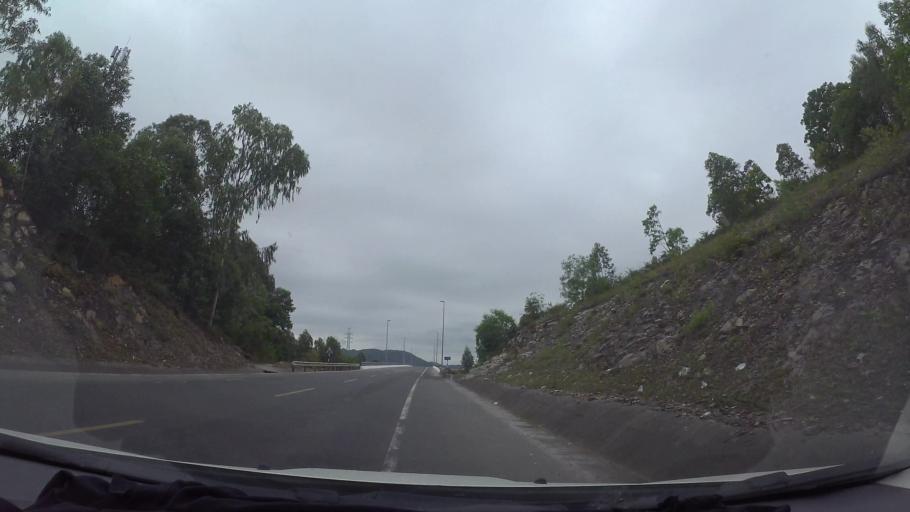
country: VN
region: Da Nang
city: Lien Chieu
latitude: 16.1168
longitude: 108.1042
